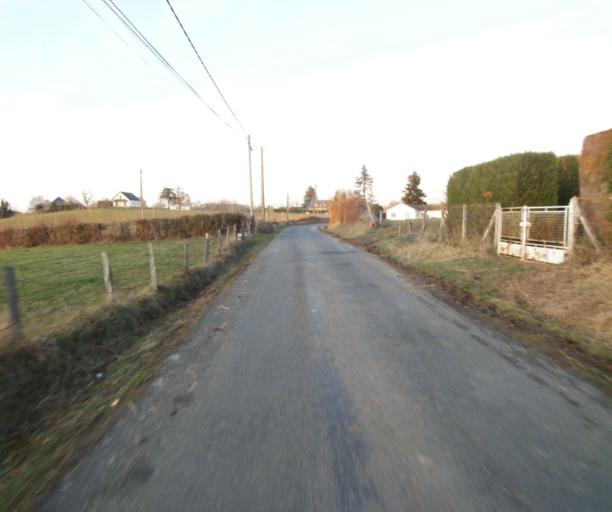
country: FR
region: Limousin
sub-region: Departement de la Correze
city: Laguenne
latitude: 45.2234
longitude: 1.8263
